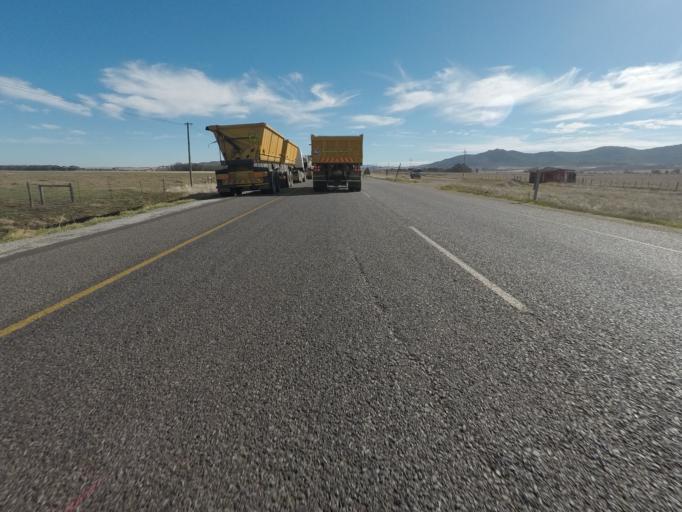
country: ZA
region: Western Cape
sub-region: West Coast District Municipality
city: Malmesbury
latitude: -33.6277
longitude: 18.7235
